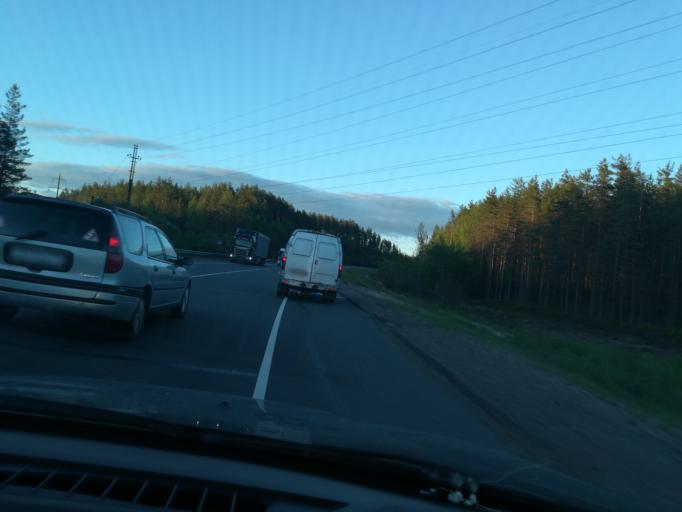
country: RU
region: Leningrad
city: Yakovlevo
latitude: 60.3620
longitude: 29.5527
